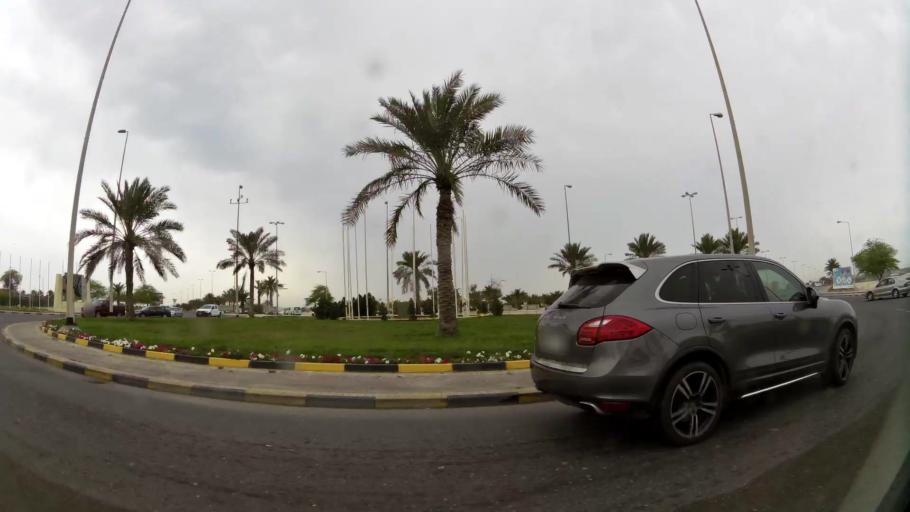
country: BH
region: Northern
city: Ar Rifa'
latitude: 26.0974
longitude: 50.5454
